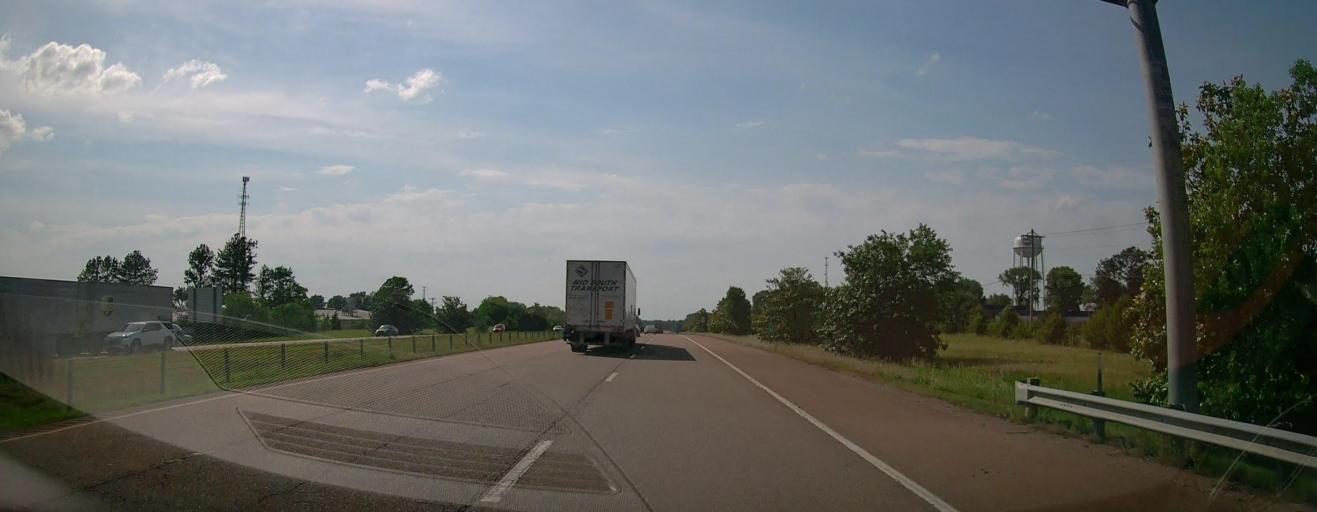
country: US
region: Mississippi
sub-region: De Soto County
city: Olive Branch
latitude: 34.9489
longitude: -89.8355
